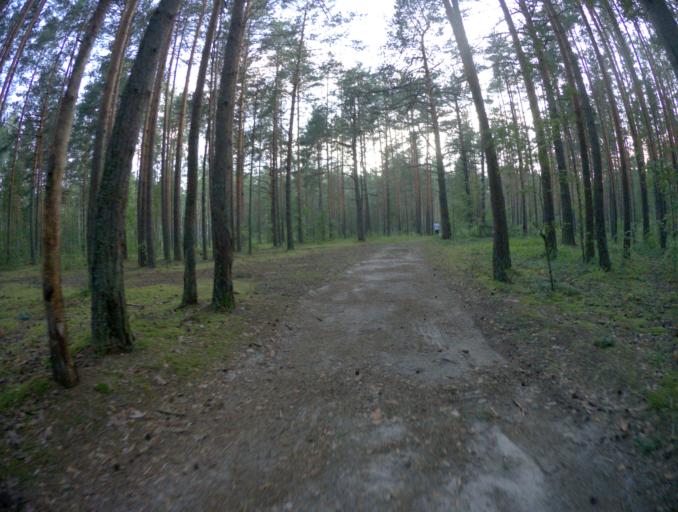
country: RU
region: Vladimir
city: Kommunar
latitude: 56.0987
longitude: 40.4619
